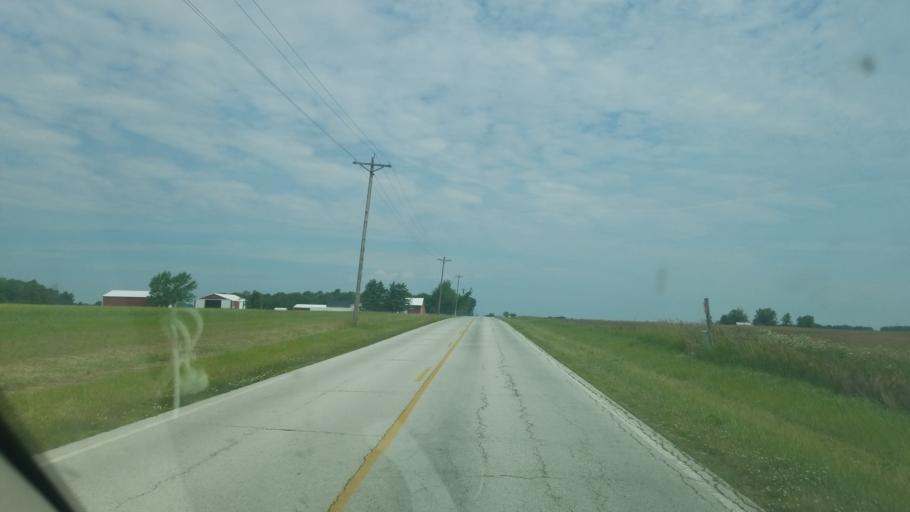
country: US
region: Ohio
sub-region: Seneca County
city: Fostoria
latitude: 41.1019
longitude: -83.4785
